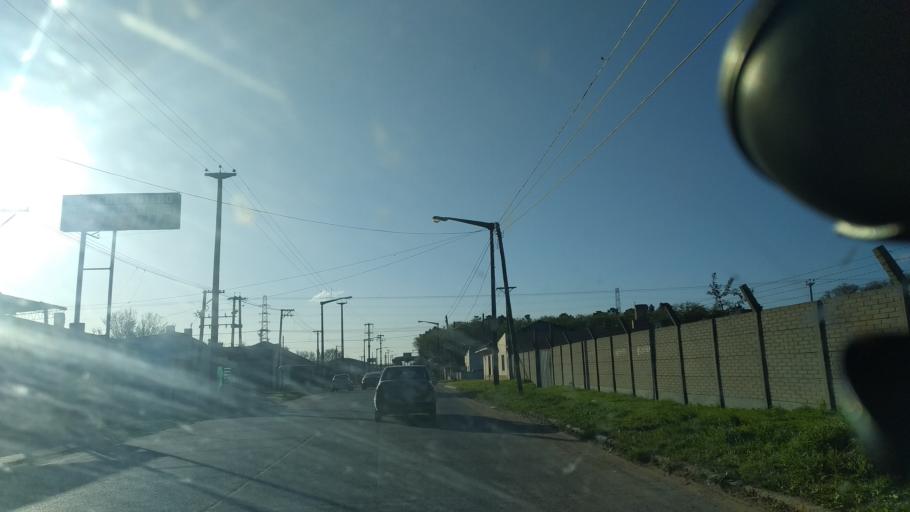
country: AR
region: Buenos Aires
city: Necochea
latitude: -38.5650
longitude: -58.7066
